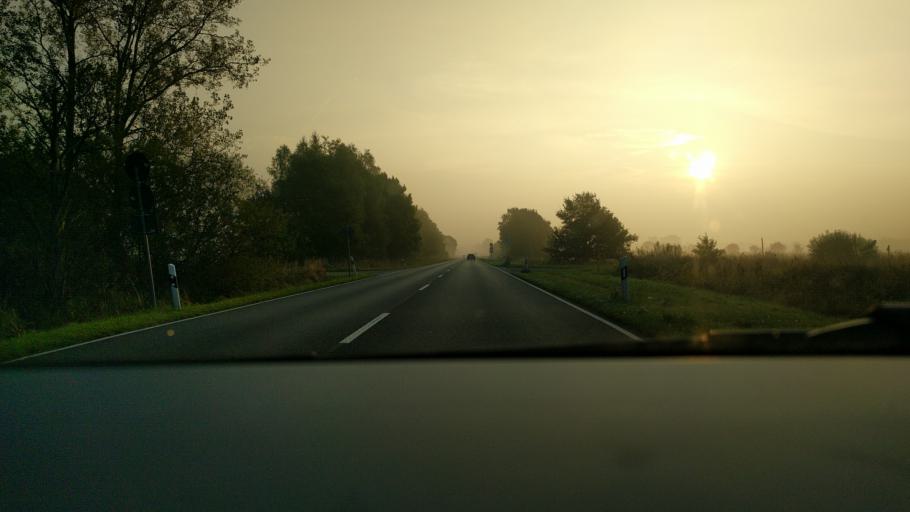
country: DE
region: Lower Saxony
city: Weyhausen
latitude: 52.4364
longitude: 10.7010
